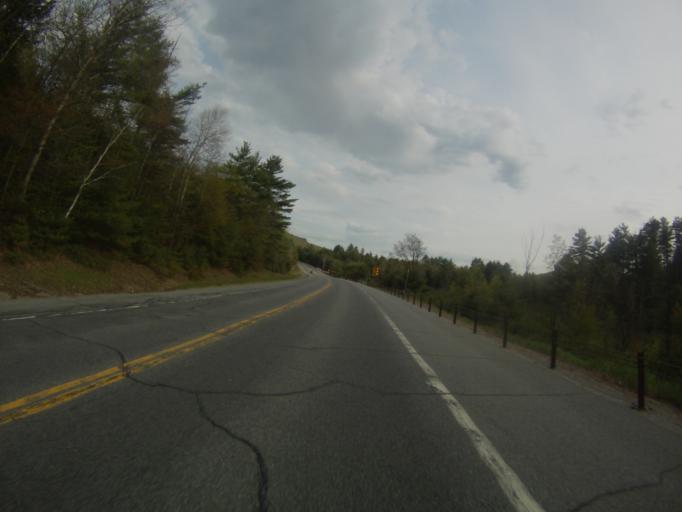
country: US
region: New York
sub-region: Warren County
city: Warrensburg
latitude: 43.6909
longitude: -73.9876
